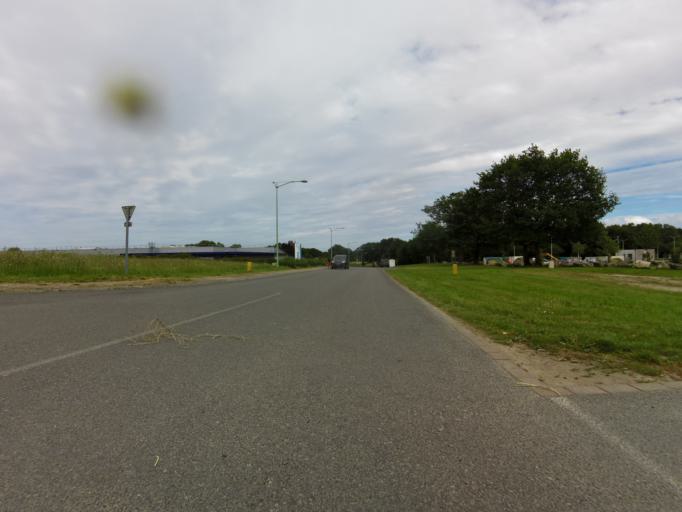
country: FR
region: Brittany
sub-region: Departement du Morbihan
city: Questembert
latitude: 47.6655
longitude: -2.4379
